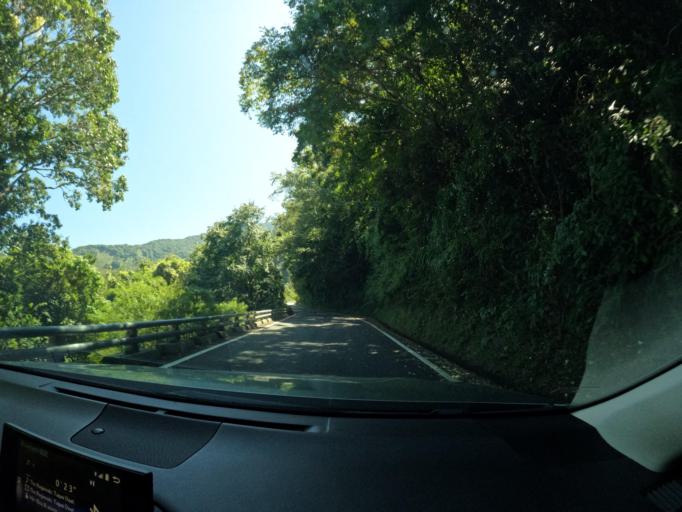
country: TW
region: Taiwan
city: Yujing
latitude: 23.2854
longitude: 120.8793
